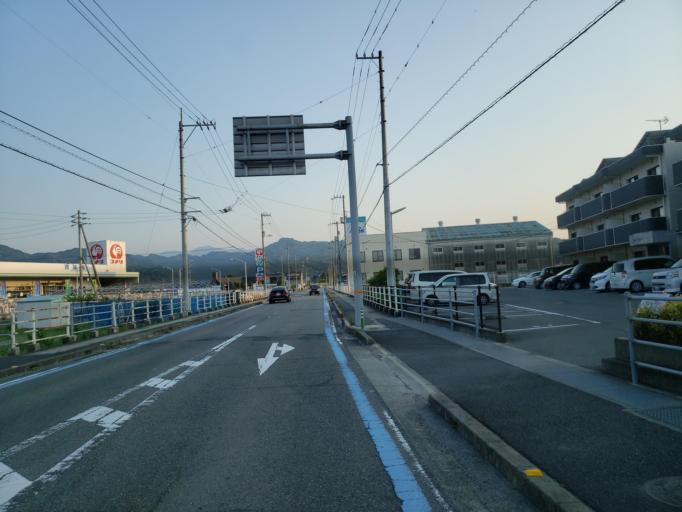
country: JP
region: Ehime
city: Hojo
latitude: 34.0379
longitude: 132.9732
